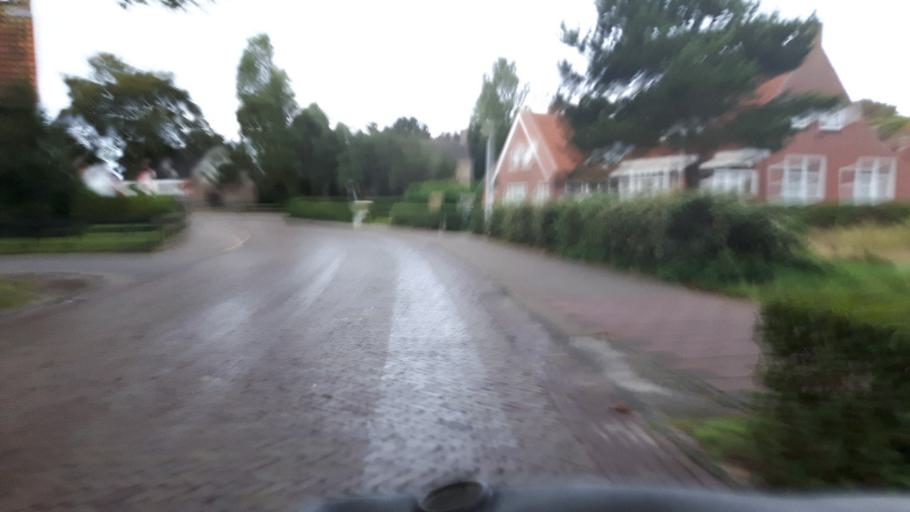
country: NL
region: Friesland
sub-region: Gemeente Ameland
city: Nes
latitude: 53.4476
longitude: 5.7699
